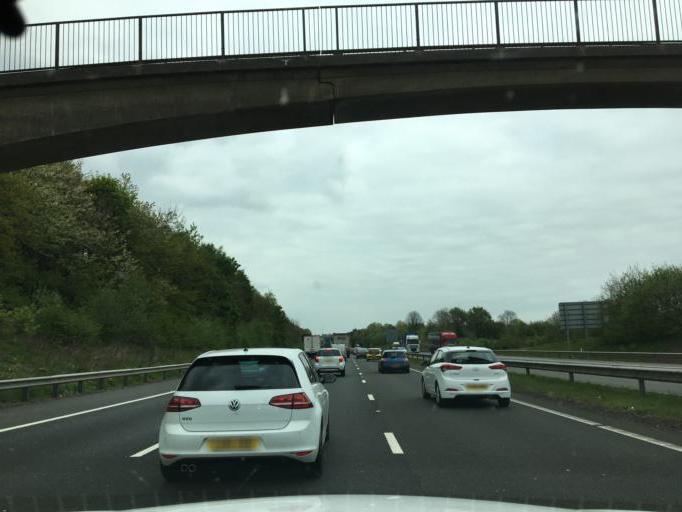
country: GB
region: Wales
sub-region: Newport
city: Marshfield
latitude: 51.5502
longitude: -3.0842
